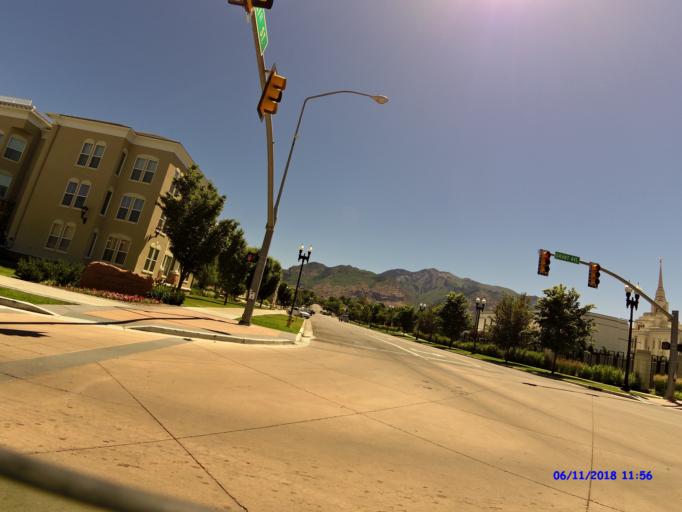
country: US
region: Utah
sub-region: Weber County
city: Ogden
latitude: 41.2292
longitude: -111.9731
